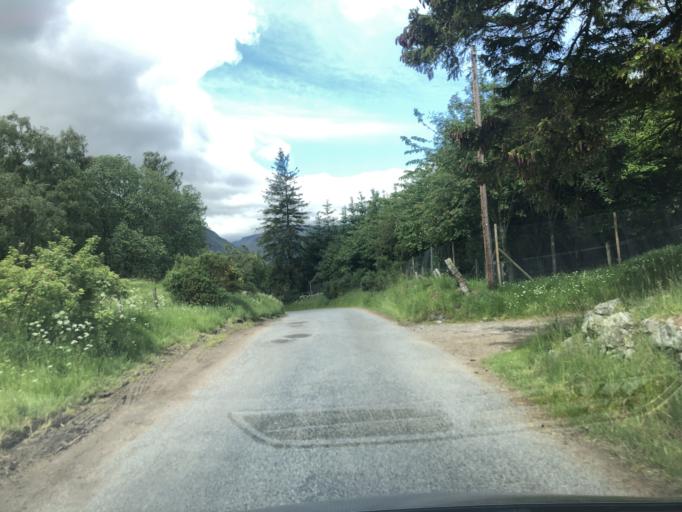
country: GB
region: Scotland
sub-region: Angus
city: Kirriemuir
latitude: 56.8382
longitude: -3.0990
